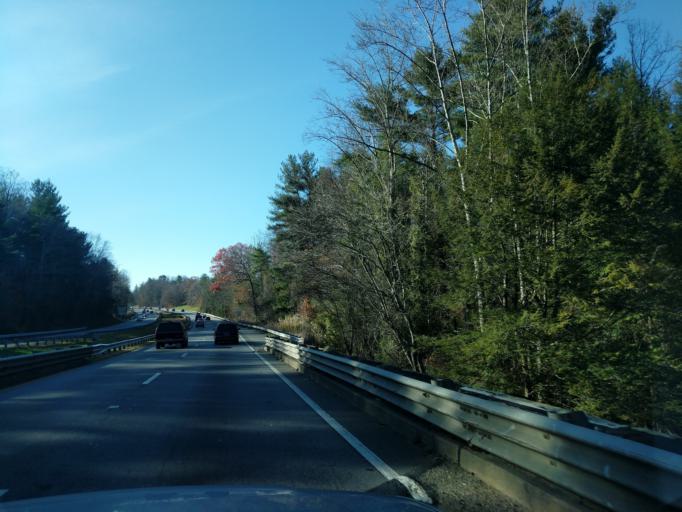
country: US
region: North Carolina
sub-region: Buncombe County
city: Biltmore Forest
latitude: 35.5581
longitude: -82.5506
